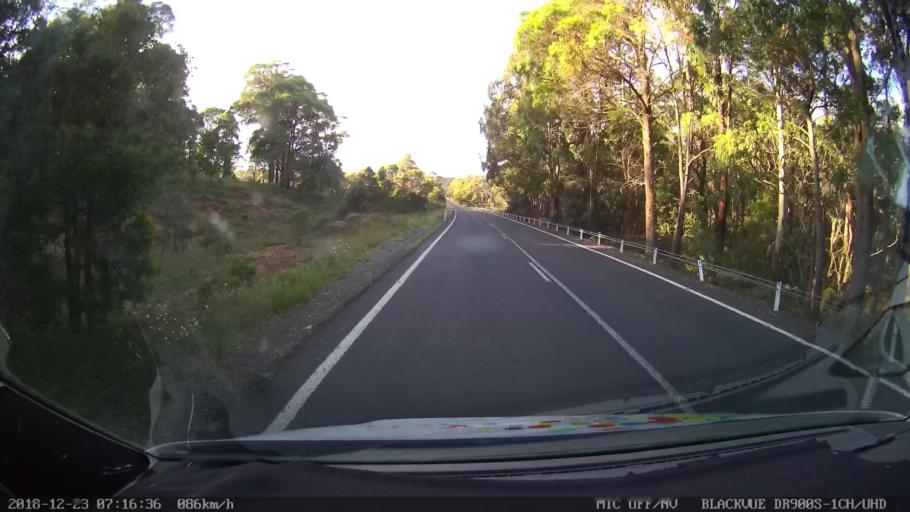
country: AU
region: New South Wales
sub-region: Bellingen
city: Dorrigo
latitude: -30.4578
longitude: 152.3085
